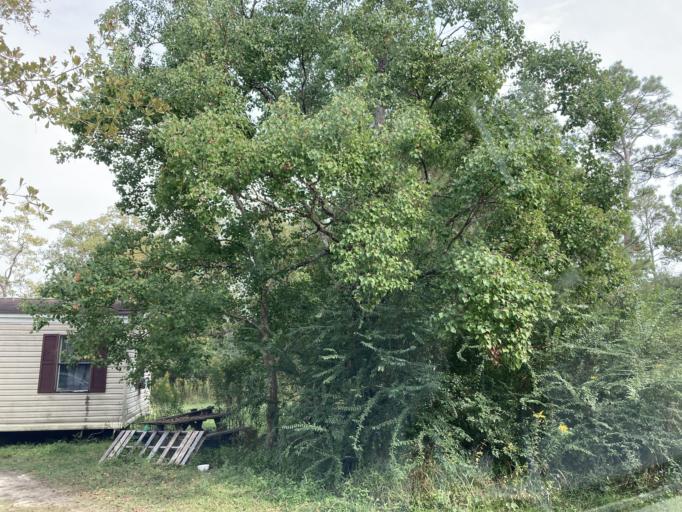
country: US
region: Mississippi
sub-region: Jackson County
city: Gulf Hills
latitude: 30.4749
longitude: -88.8429
